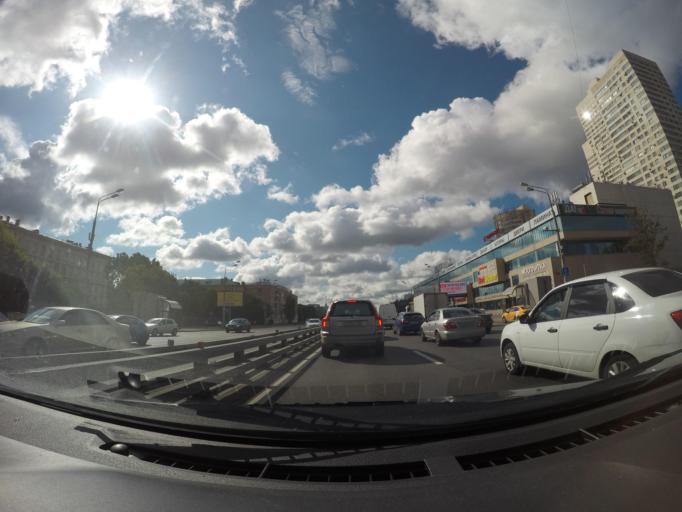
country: RU
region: Moskovskaya
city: Levoberezhnyy
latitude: 55.8293
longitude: 37.4894
